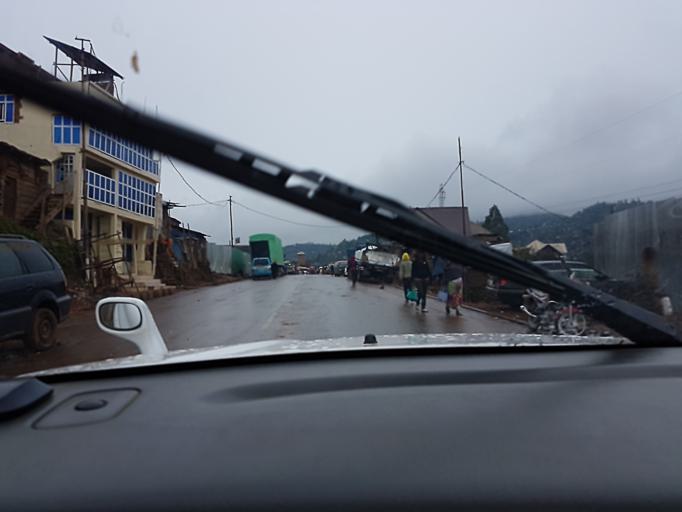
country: CD
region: South Kivu
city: Bukavu
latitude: -2.5199
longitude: 28.8550
